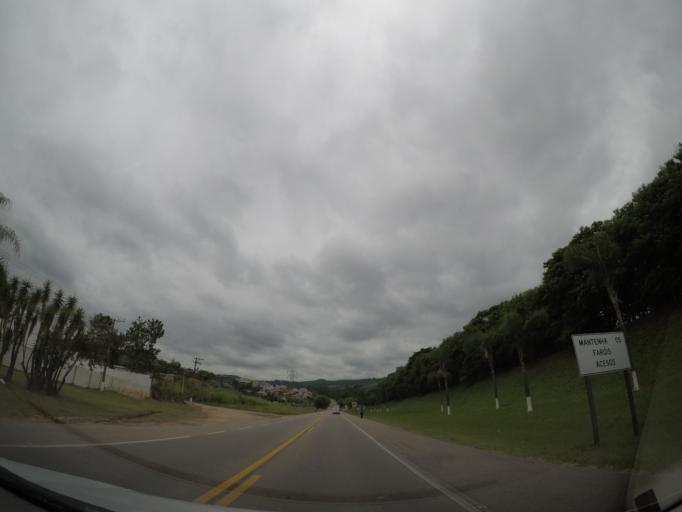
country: BR
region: Sao Paulo
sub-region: Louveira
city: Louveira
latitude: -23.0711
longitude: -46.9517
